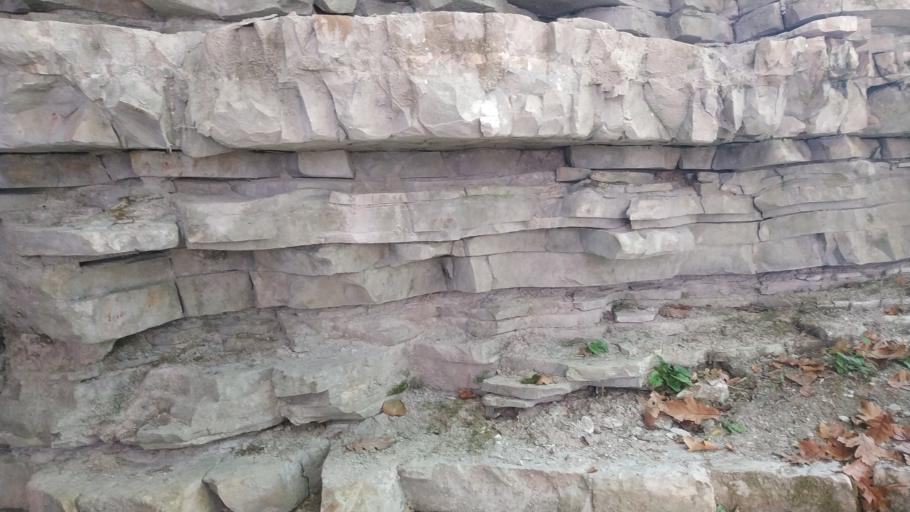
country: RU
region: Krasnodarskiy
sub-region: Sochi City
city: Lazarevskoye
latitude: 43.9836
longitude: 39.4094
